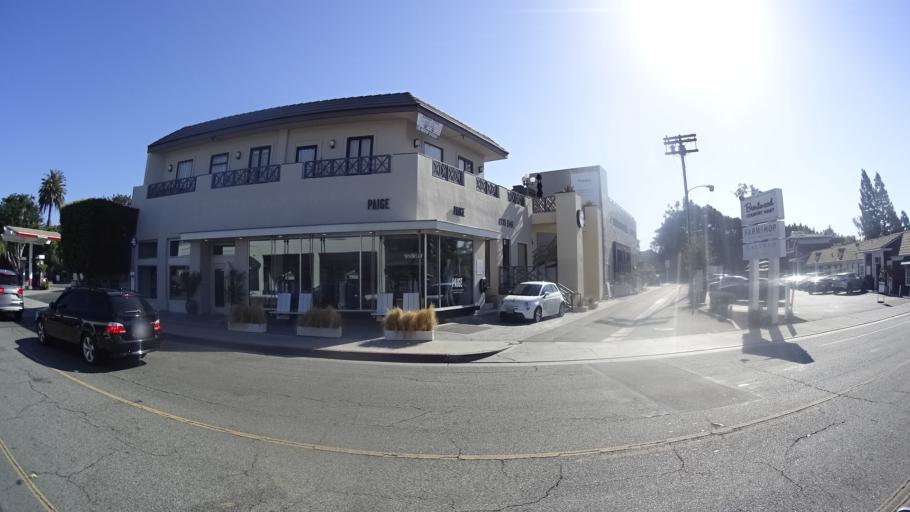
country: US
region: California
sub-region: Los Angeles County
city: Santa Monica
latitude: 34.0478
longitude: -118.4914
